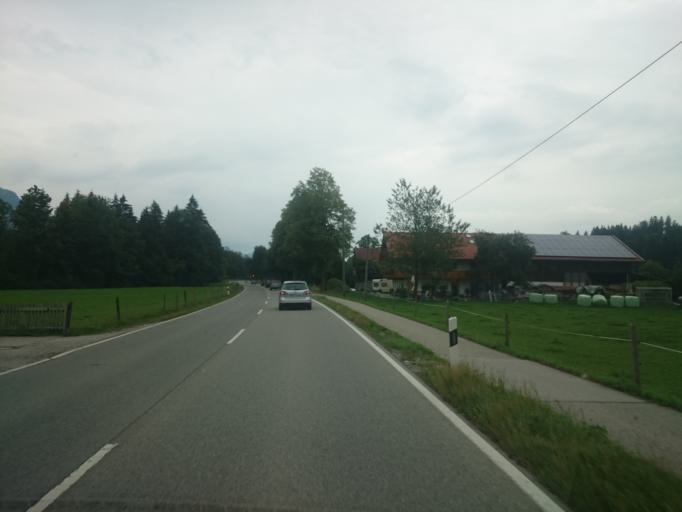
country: DE
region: Bavaria
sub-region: Upper Bavaria
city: Lenggries
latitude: 47.6427
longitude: 11.5924
